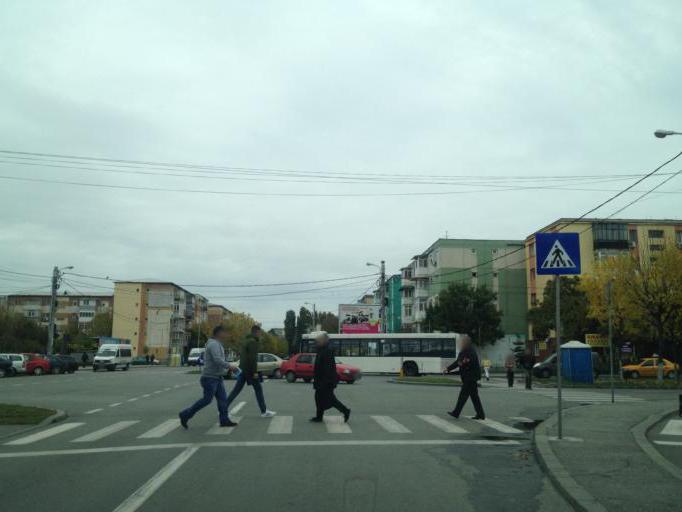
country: RO
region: Dolj
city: Craiova
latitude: 44.3372
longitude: 23.7758
